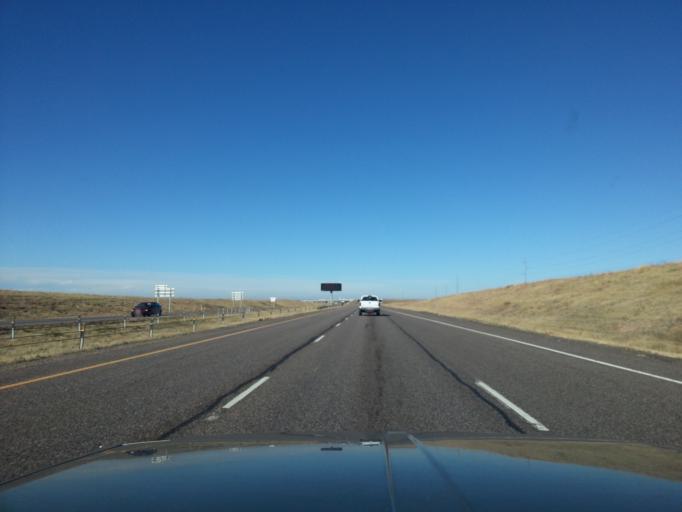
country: US
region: Colorado
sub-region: Adams County
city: Brighton
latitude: 39.8909
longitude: -104.7617
